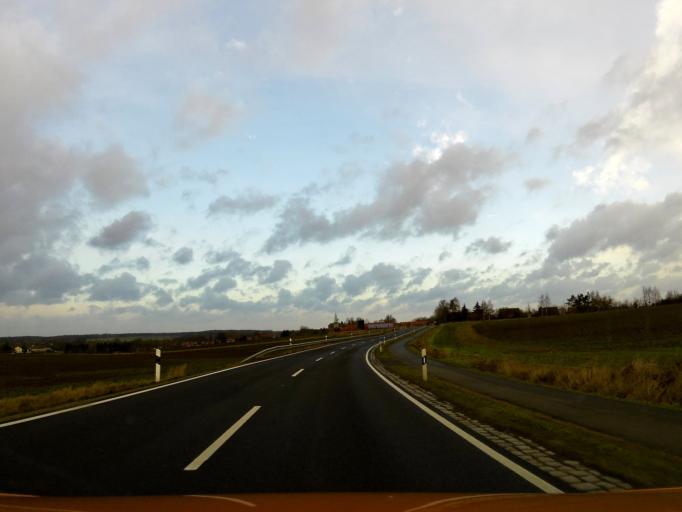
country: DE
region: Lower Saxony
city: Gross Twulpstedt
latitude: 52.3671
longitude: 10.9209
